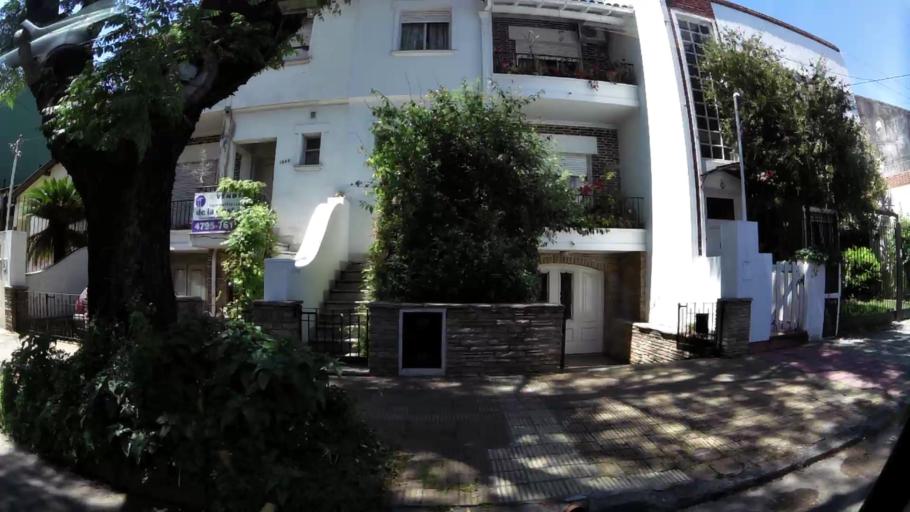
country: AR
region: Buenos Aires
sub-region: Partido de Vicente Lopez
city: Olivos
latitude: -34.5087
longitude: -58.4932
